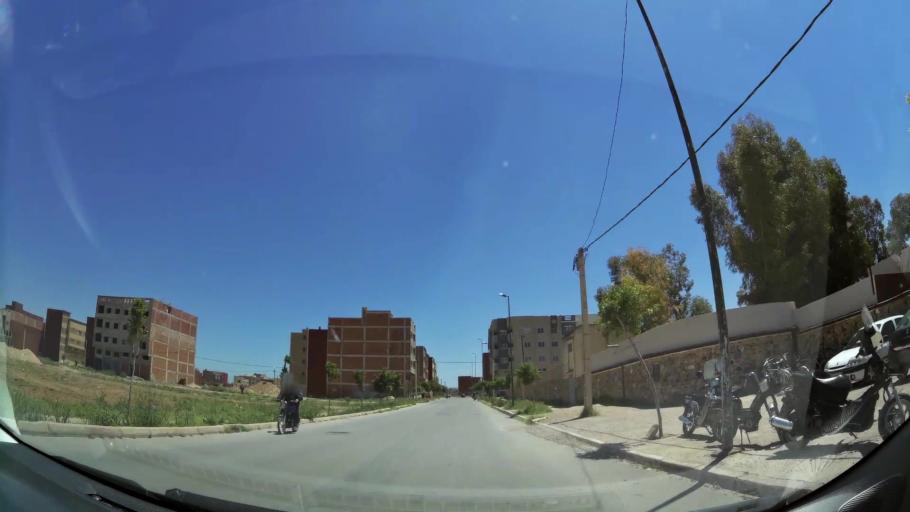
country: MA
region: Oriental
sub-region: Oujda-Angad
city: Oujda
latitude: 34.6702
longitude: -1.8810
